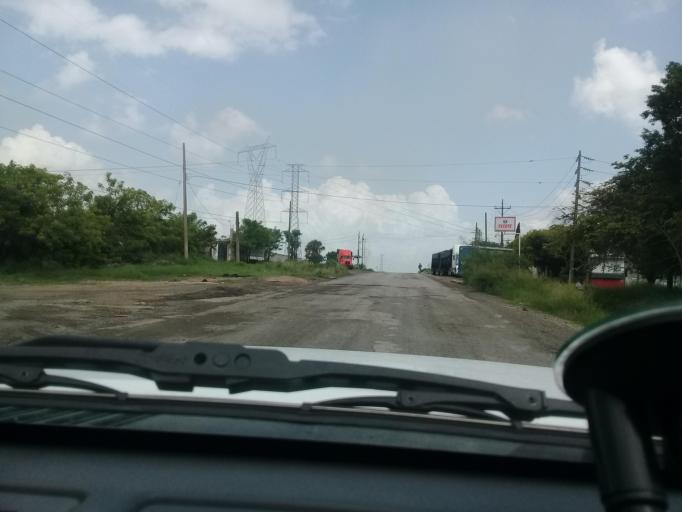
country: MX
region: Veracruz
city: Moralillo
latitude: 22.2195
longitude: -98.0034
